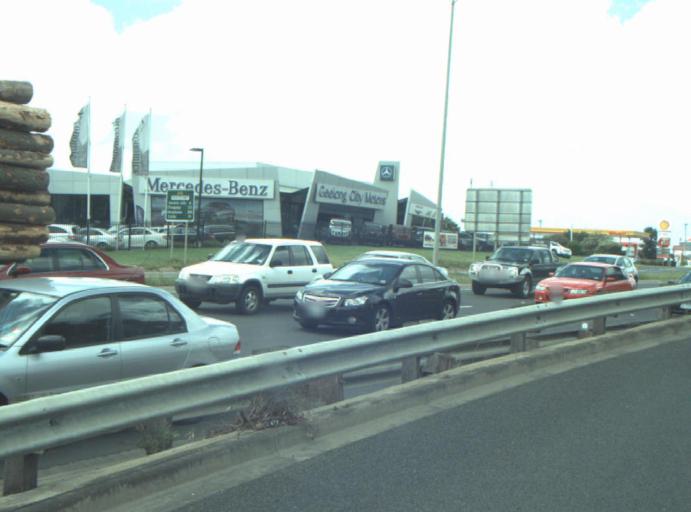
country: AU
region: Victoria
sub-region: Greater Geelong
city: Breakwater
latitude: -38.1756
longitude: 144.3521
